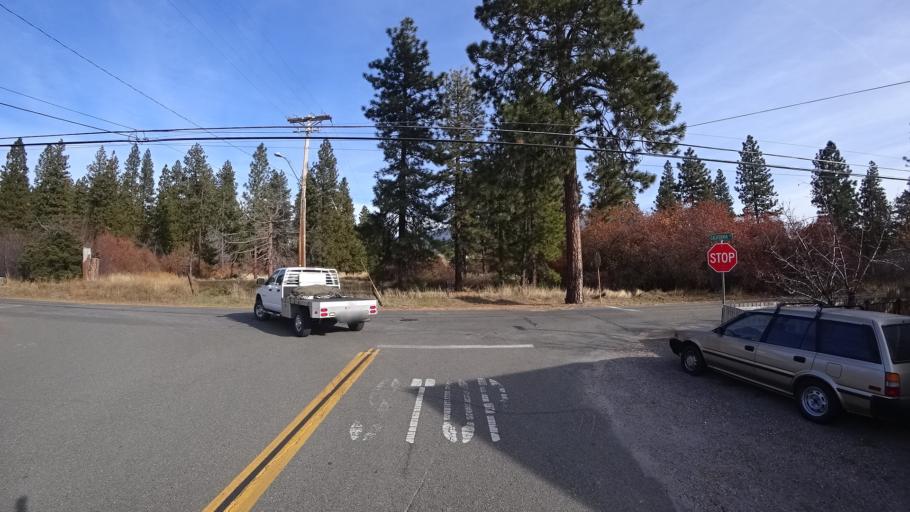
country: US
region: California
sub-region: Siskiyou County
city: Weed
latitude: 41.4392
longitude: -122.3768
